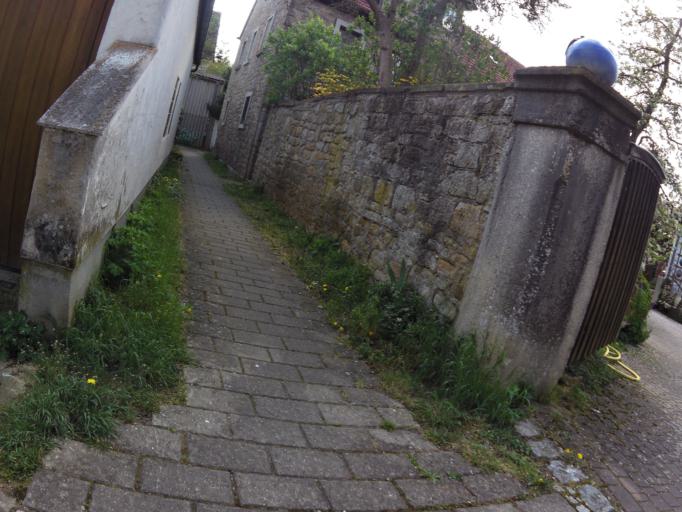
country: DE
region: Bavaria
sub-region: Regierungsbezirk Unterfranken
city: Giebelstadt
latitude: 49.6724
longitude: 9.9602
